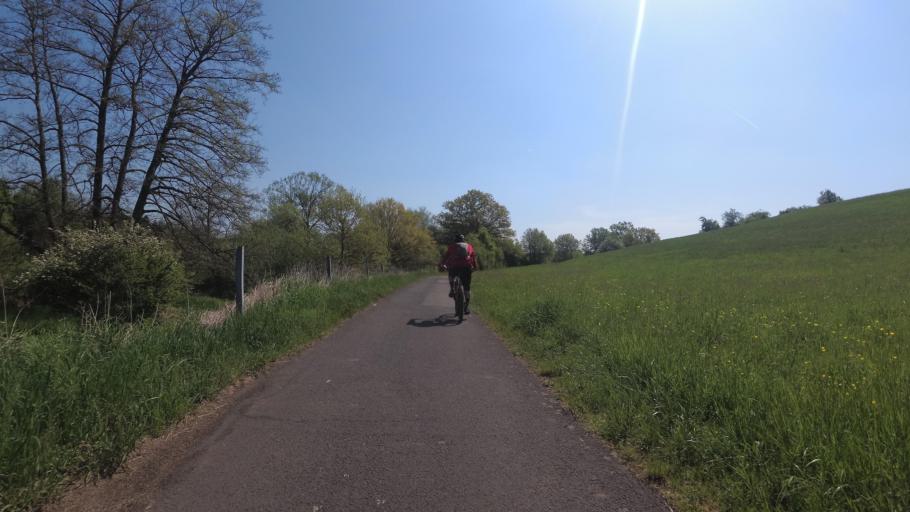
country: DE
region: Rheinland-Pfalz
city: Niedermohr
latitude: 49.4570
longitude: 7.4690
